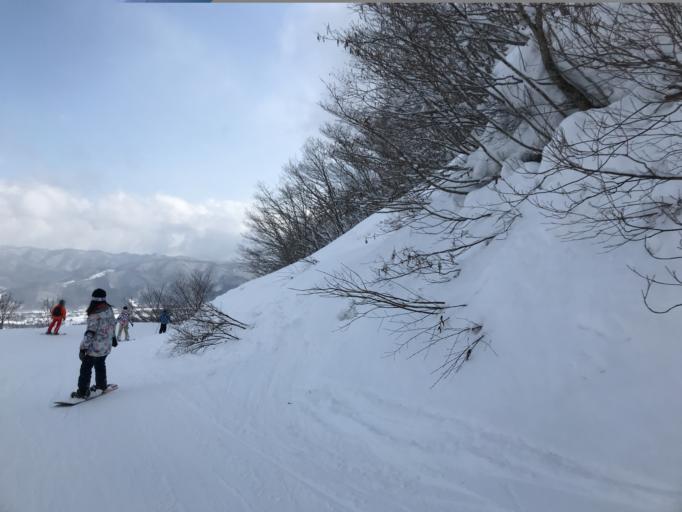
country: JP
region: Nagano
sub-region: Kitaazumi Gun
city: Hakuba
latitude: 36.7093
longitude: 137.8239
